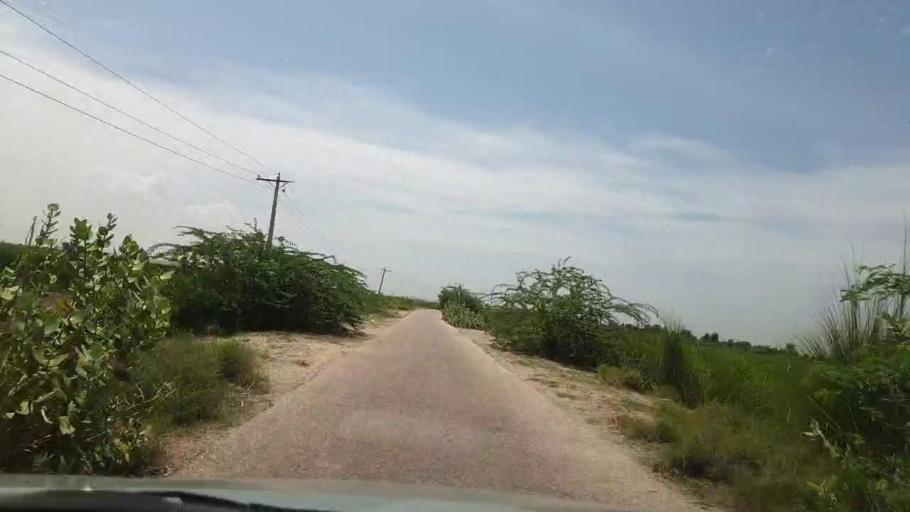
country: PK
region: Sindh
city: Bozdar
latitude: 27.0617
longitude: 68.9824
